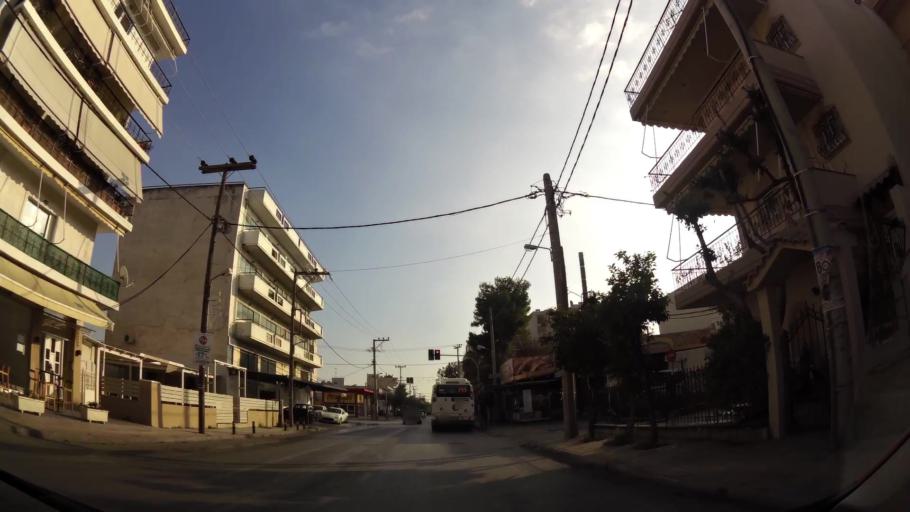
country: GR
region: Attica
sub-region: Nomarchia Anatolikis Attikis
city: Acharnes
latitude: 38.0846
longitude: 23.7452
